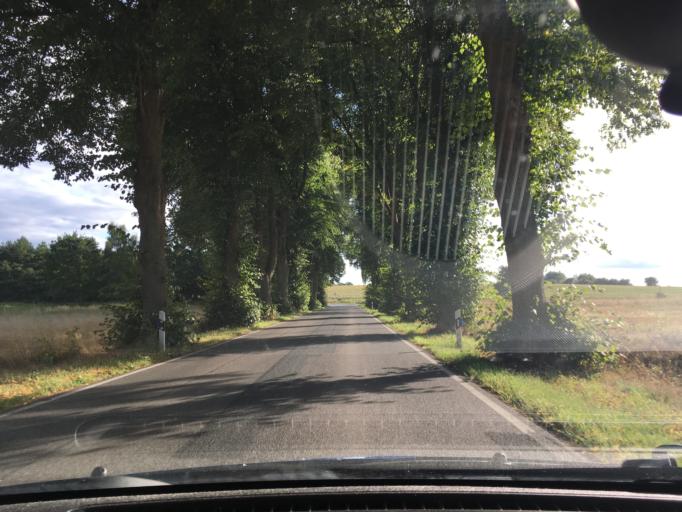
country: DE
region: Lower Saxony
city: Stelle
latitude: 53.3403
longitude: 10.0826
